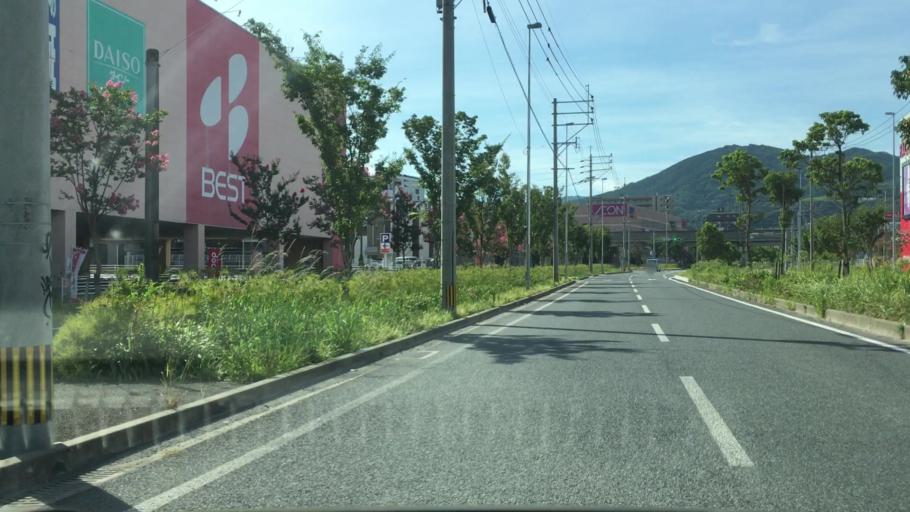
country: JP
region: Fukuoka
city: Maebaru-chuo
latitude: 33.5791
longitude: 130.2545
